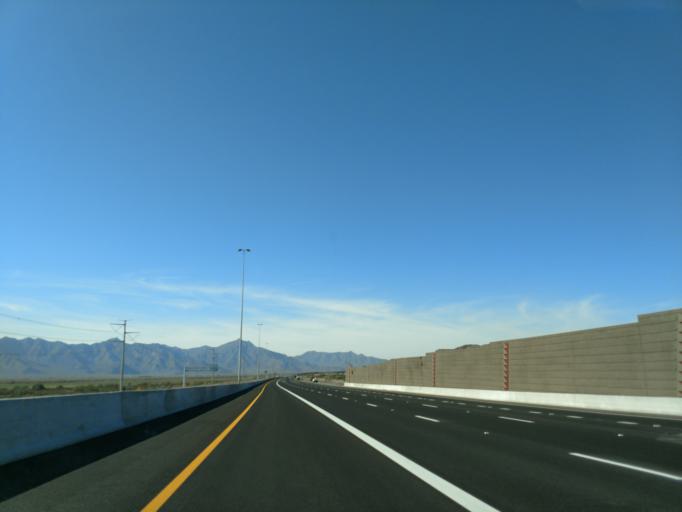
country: US
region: Arizona
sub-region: Maricopa County
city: Laveen
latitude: 33.2920
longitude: -112.1015
